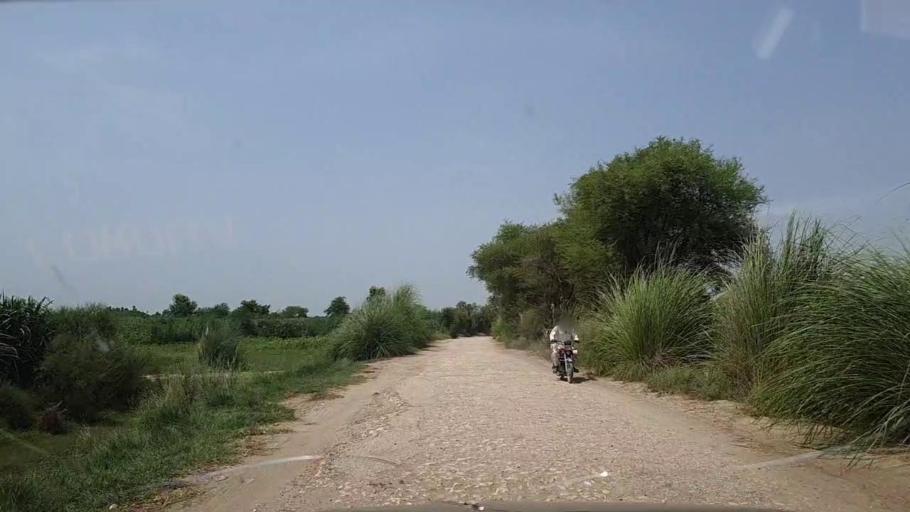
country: PK
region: Sindh
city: Ghotki
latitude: 28.0794
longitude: 69.3199
